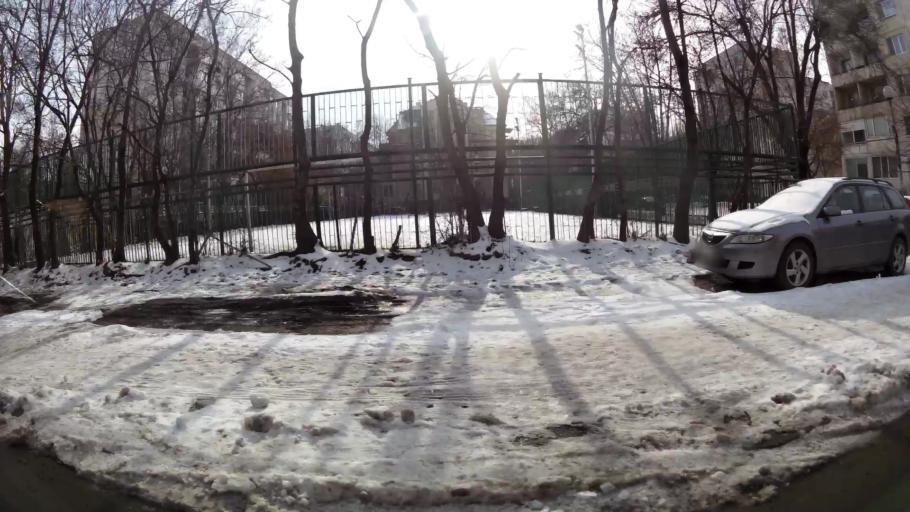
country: BG
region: Sofia-Capital
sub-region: Stolichna Obshtina
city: Sofia
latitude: 42.7055
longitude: 23.3490
